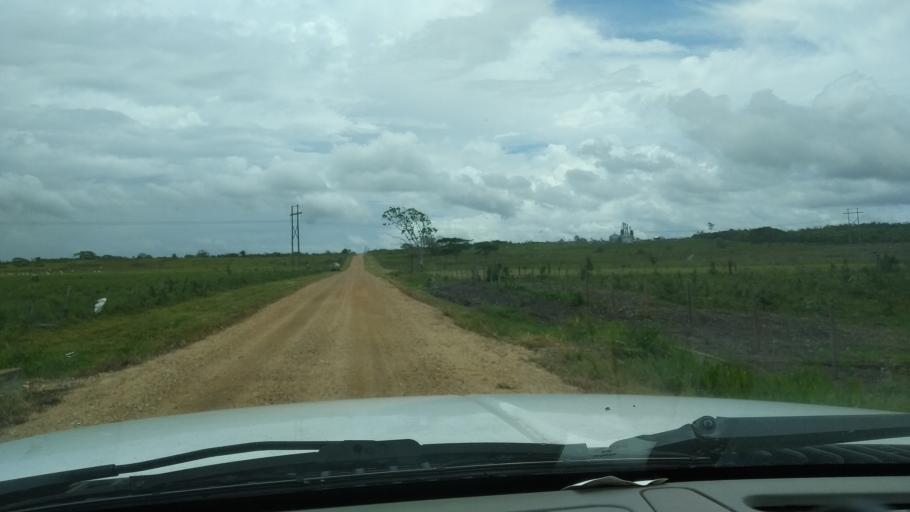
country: BZ
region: Cayo
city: San Ignacio
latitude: 17.2301
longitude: -88.9723
